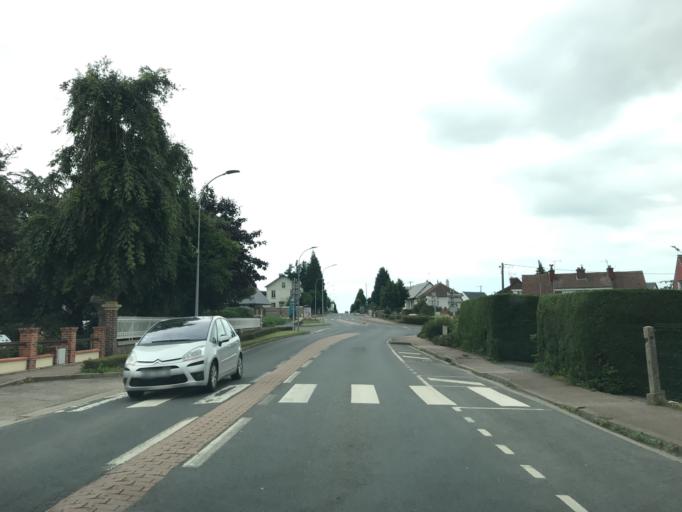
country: FR
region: Haute-Normandie
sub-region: Departement de la Seine-Maritime
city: Breaute
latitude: 49.6271
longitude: 0.3983
